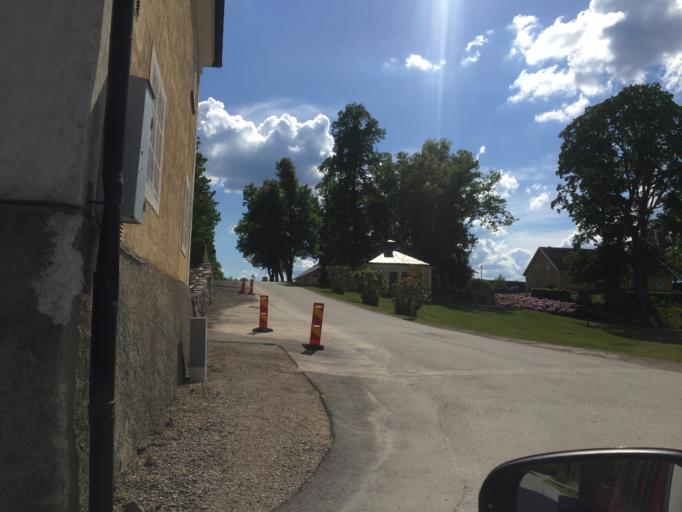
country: SE
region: Soedermanland
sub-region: Katrineholms Kommun
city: Katrineholm
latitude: 58.9333
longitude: 16.3784
